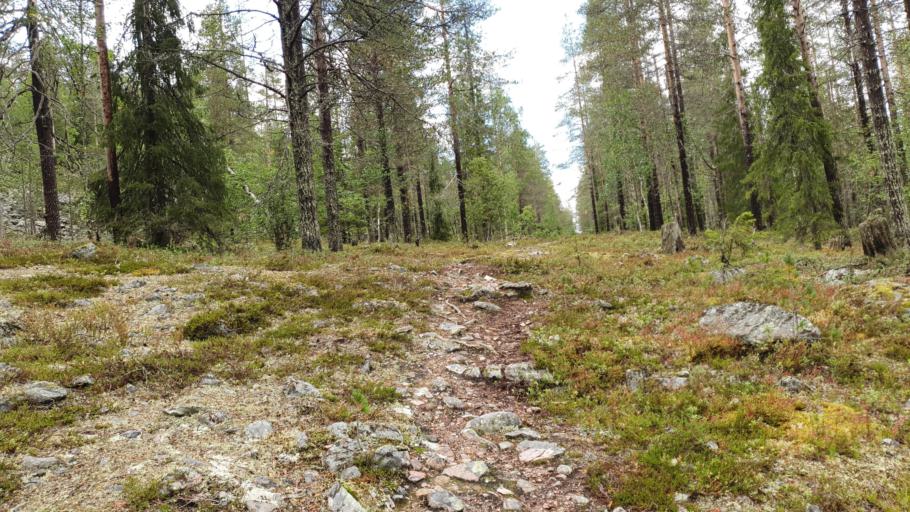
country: FI
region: Lapland
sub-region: Tunturi-Lappi
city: Kolari
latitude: 67.6003
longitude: 24.1126
